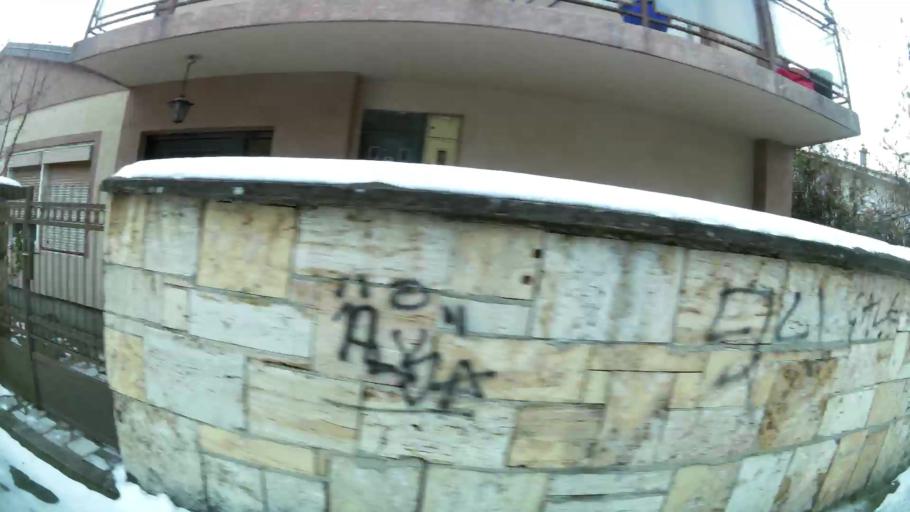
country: MK
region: Butel
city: Butel
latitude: 42.0306
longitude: 21.4431
